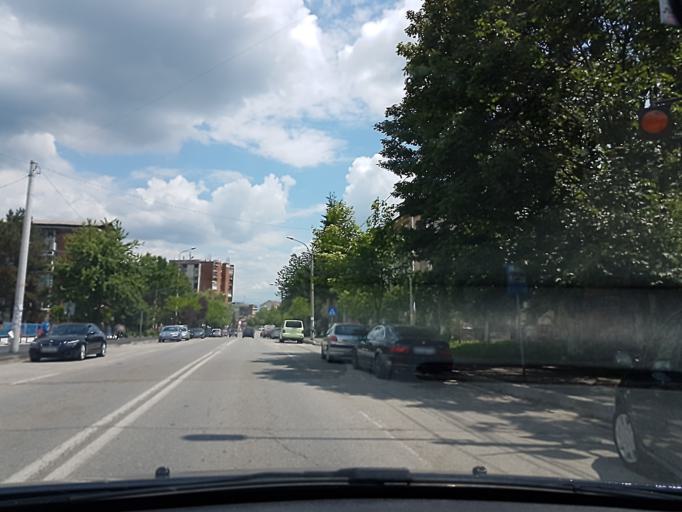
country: RO
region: Hunedoara
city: Lupeni
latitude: 45.3534
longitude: 23.2082
